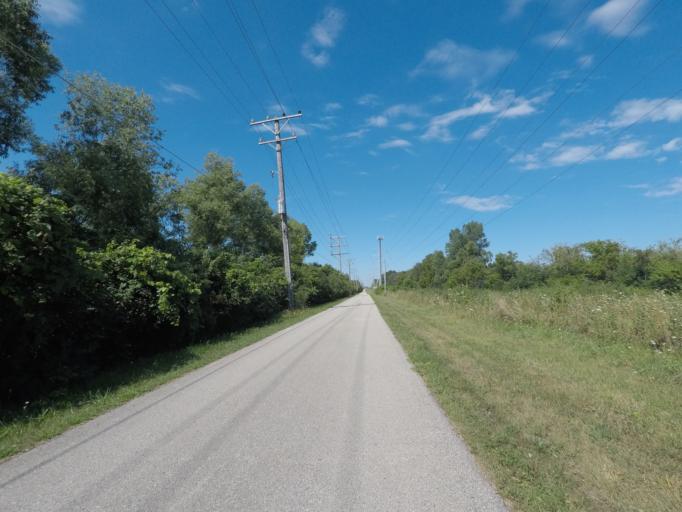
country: US
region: Wisconsin
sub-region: Waukesha County
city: Waukesha
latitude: 43.0099
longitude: -88.1767
